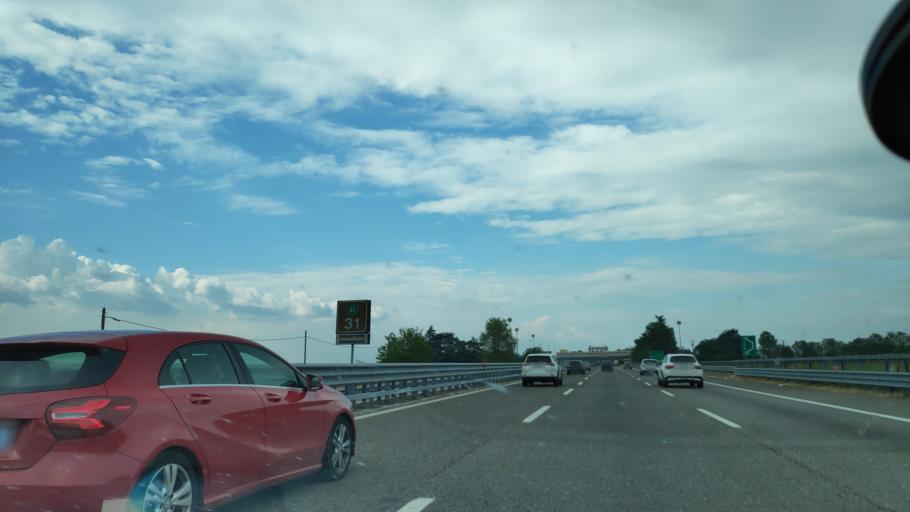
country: IT
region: Lombardy
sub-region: Provincia di Pavia
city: Gropello Cairoli
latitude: 45.1432
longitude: 8.9886
